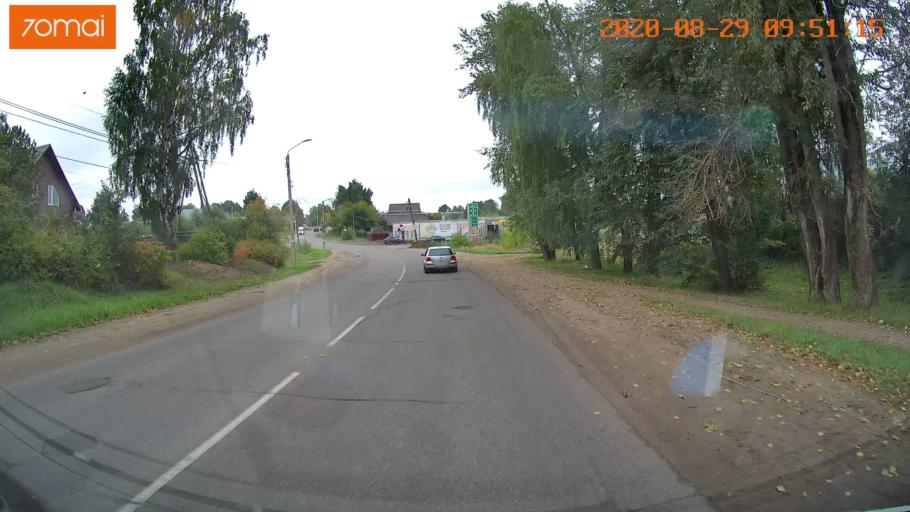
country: RU
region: Ivanovo
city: Kineshma
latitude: 57.4307
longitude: 42.1967
